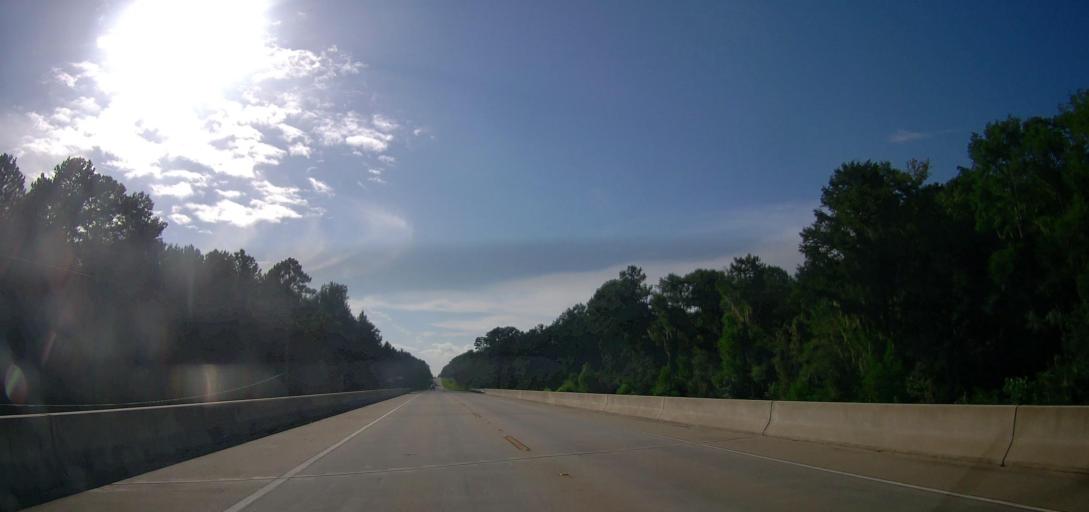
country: US
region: Georgia
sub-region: Coffee County
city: Douglas
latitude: 31.4686
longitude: -82.7666
